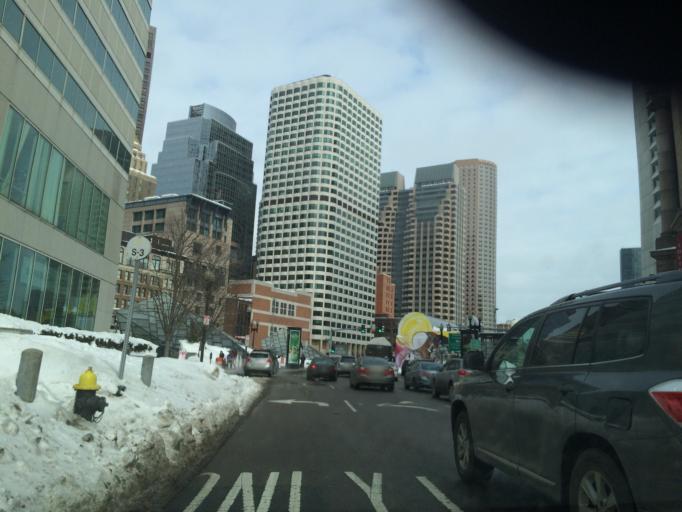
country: US
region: Massachusetts
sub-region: Suffolk County
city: Boston
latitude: 42.3519
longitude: -71.0558
